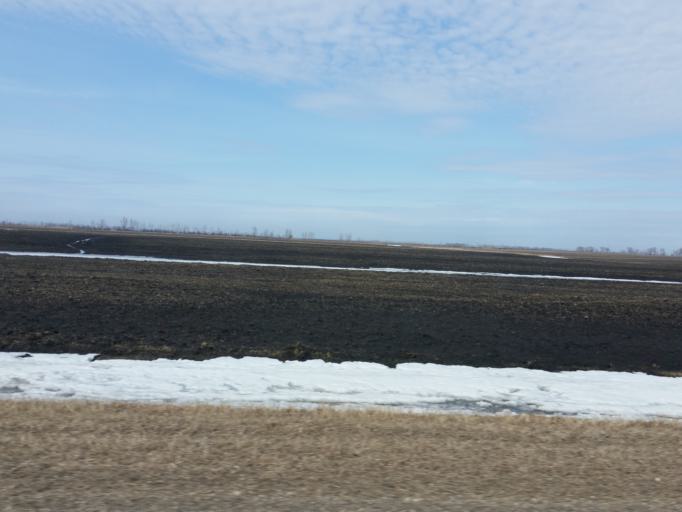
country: US
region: North Dakota
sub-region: Walsh County
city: Grafton
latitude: 48.4265
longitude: -97.2403
